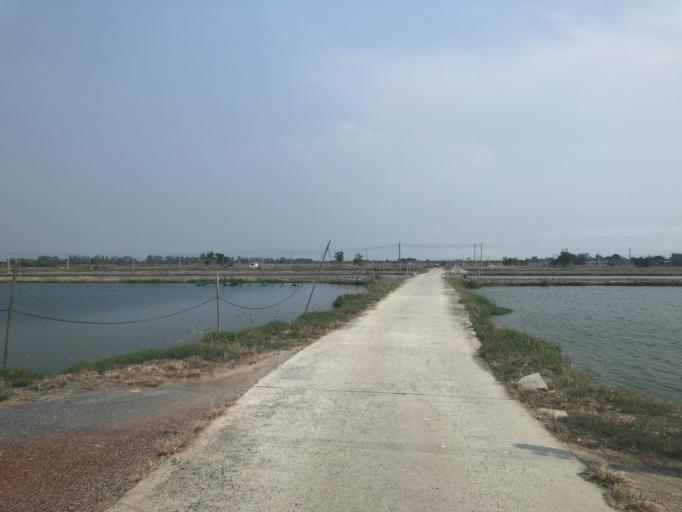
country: TH
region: Chachoengsao
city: Bang Pakong
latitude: 13.5226
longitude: 100.9114
